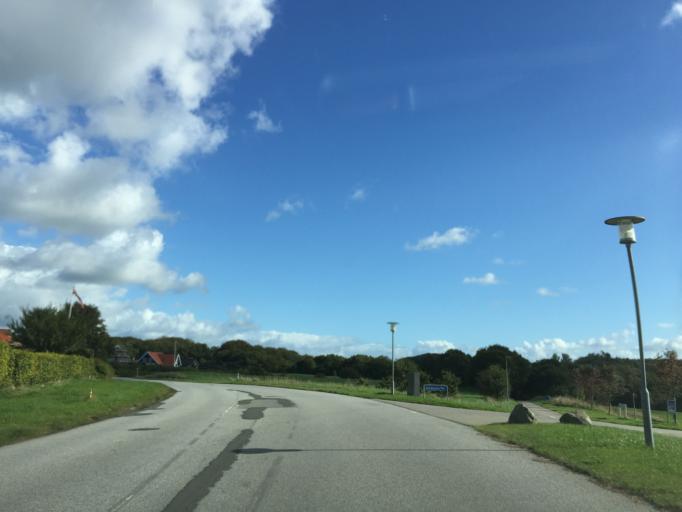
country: DK
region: Central Jutland
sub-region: Viborg Kommune
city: Viborg
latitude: 56.4451
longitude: 9.4496
